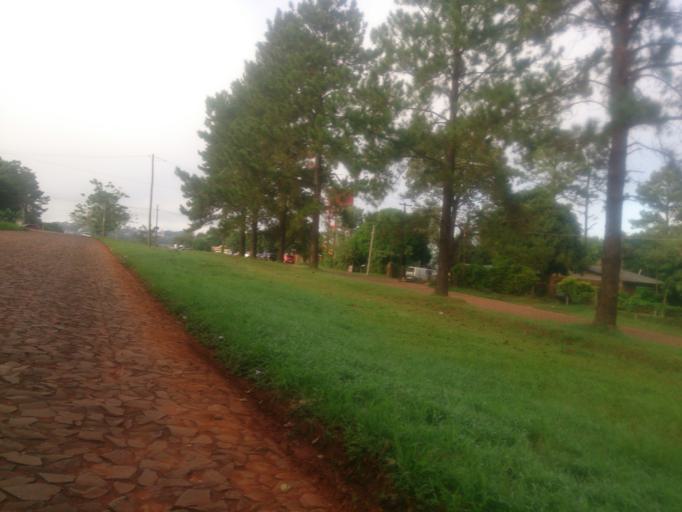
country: AR
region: Misiones
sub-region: Departamento de Obera
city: Obera
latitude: -27.4728
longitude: -55.1063
